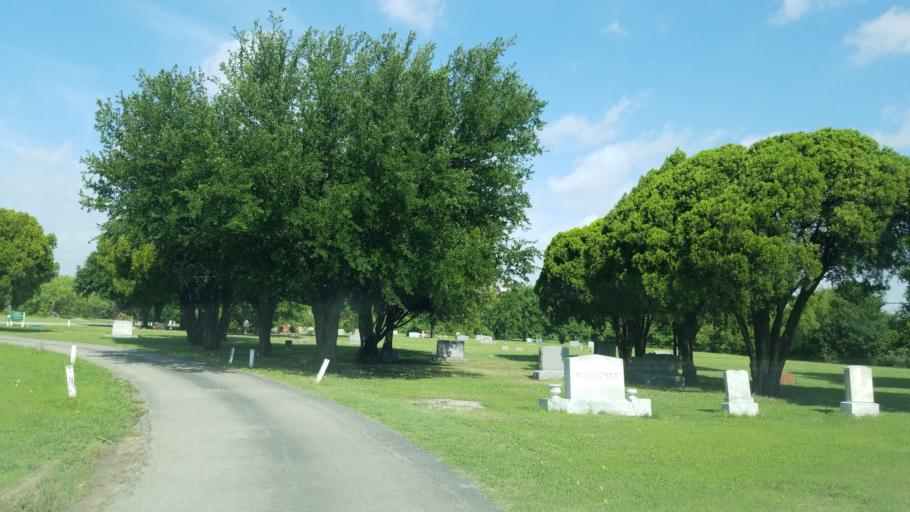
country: US
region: Texas
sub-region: Dallas County
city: Farmers Branch
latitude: 32.8804
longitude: -96.8868
